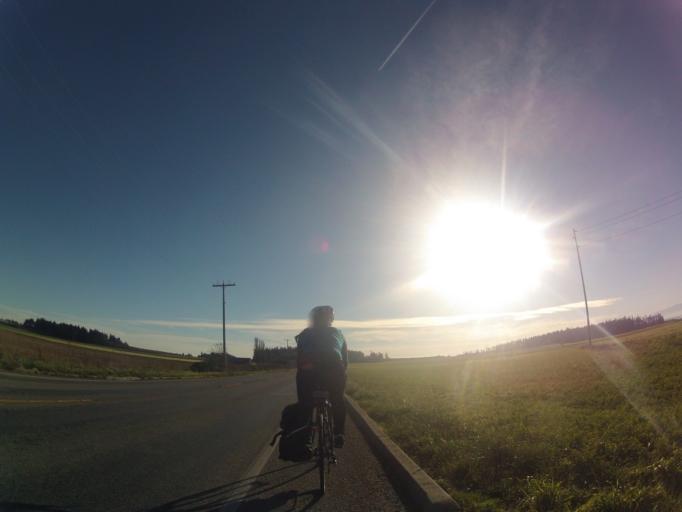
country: US
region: Washington
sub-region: Island County
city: Coupeville
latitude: 48.1986
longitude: -122.6862
